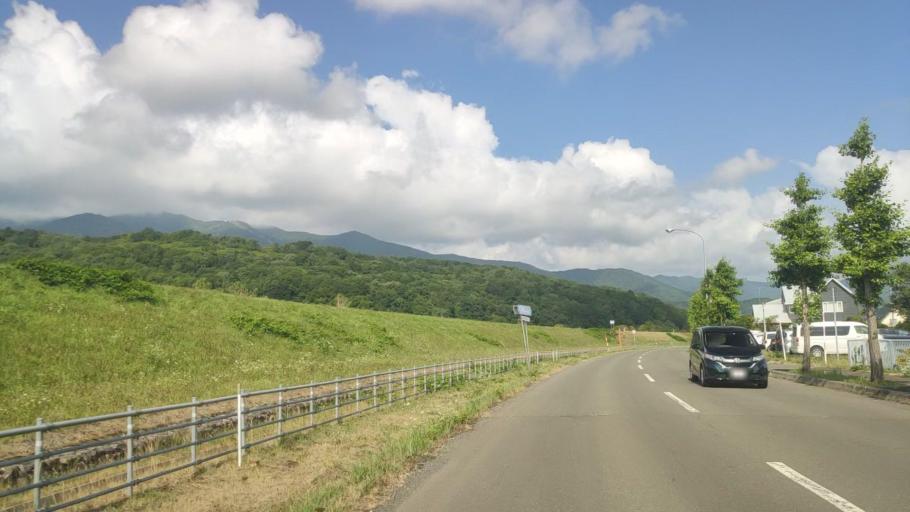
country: JP
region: Hokkaido
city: Shimo-furano
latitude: 43.3397
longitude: 142.3816
